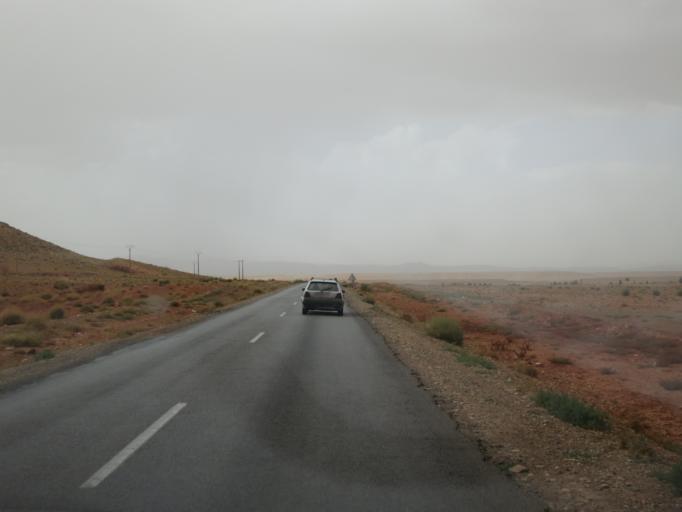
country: MA
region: Meknes-Tafilalet
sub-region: Khenifra
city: Itzer
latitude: 32.8659
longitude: -4.9444
